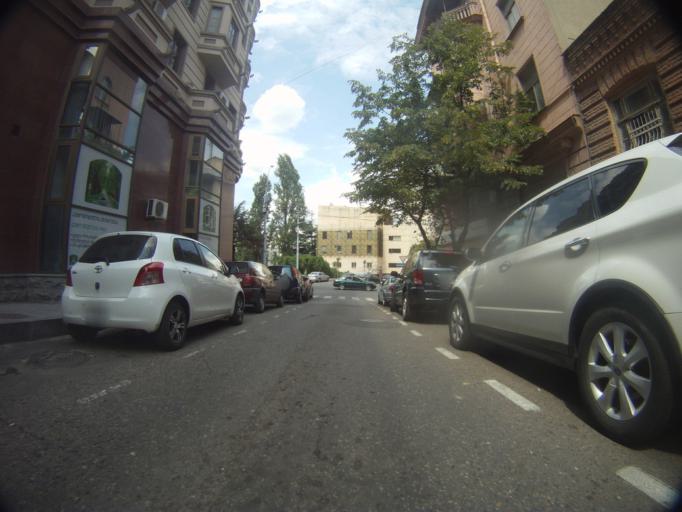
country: GE
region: T'bilisi
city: Tbilisi
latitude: 41.7061
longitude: 44.7842
